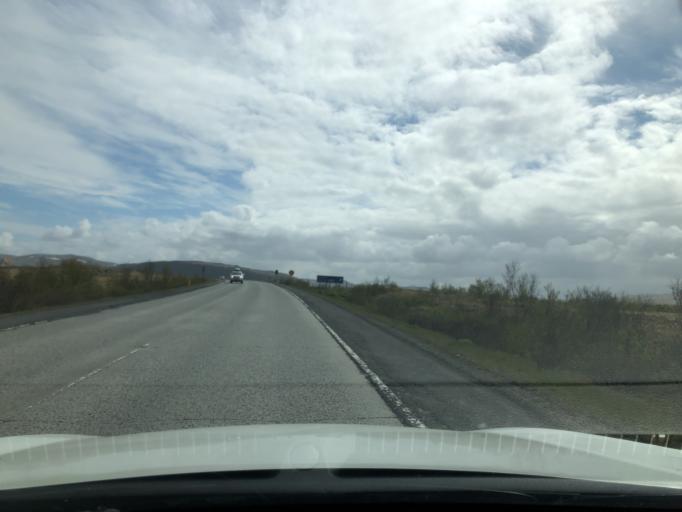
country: IS
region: Capital Region
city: Mosfellsbaer
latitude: 64.1979
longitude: -21.7061
